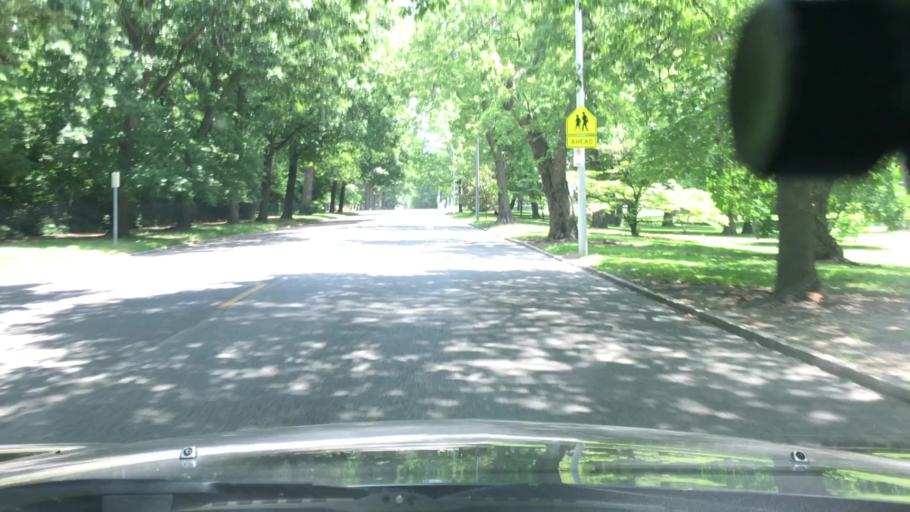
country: US
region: Missouri
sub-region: Saint Louis County
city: Richmond Heights
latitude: 38.6089
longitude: -90.2597
